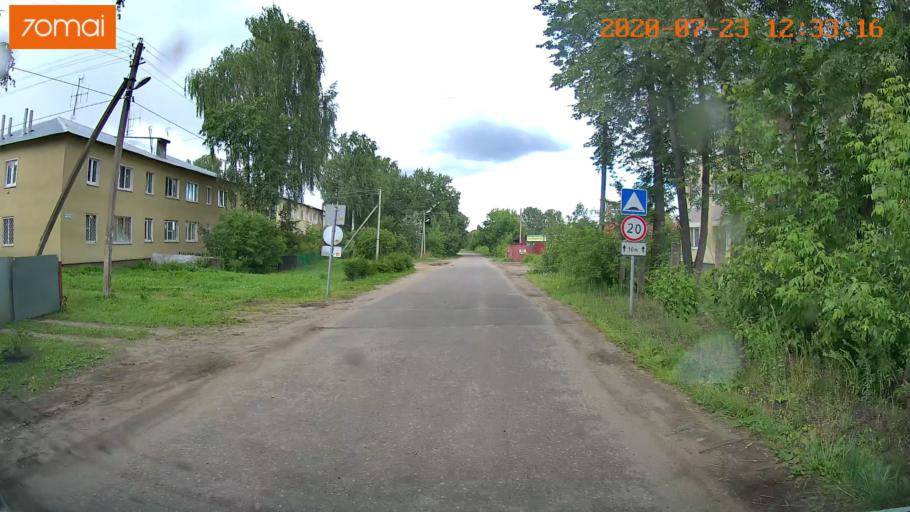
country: RU
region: Ivanovo
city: Bogorodskoye
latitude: 57.0484
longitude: 41.0080
